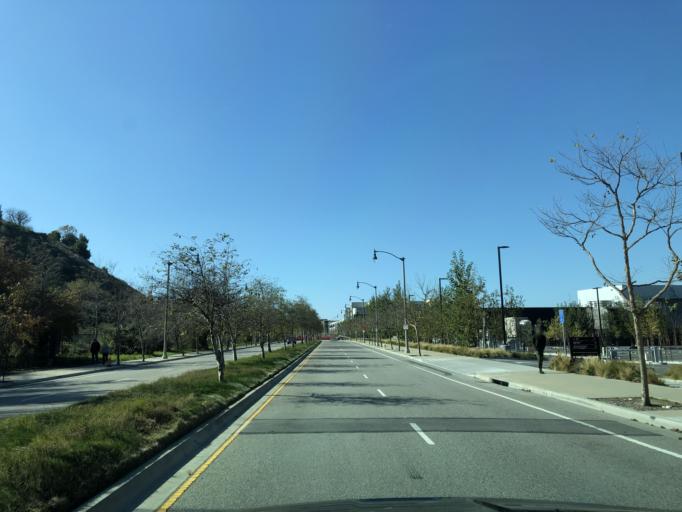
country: US
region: California
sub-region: Los Angeles County
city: Ladera Heights
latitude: 33.9766
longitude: -118.4089
